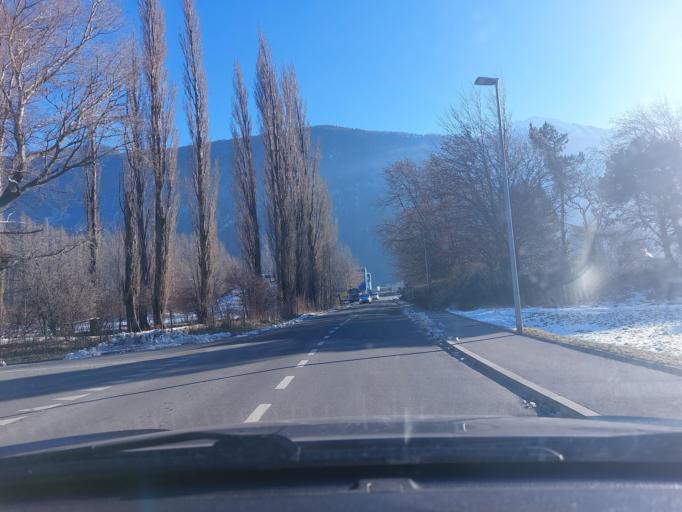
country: CH
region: Valais
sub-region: Martigny District
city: Martigny-Ville
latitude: 46.1105
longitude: 7.0854
